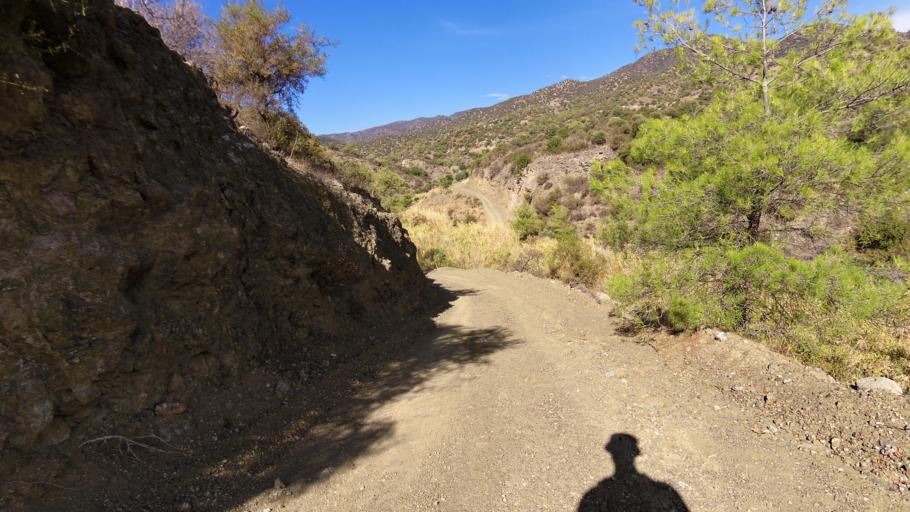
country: CY
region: Limassol
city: Mouttagiaka
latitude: 34.7753
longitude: 33.0727
